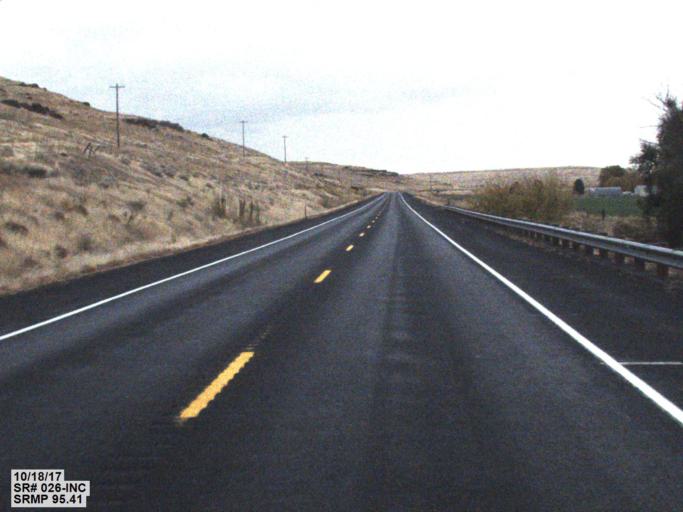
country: US
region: Washington
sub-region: Columbia County
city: Dayton
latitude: 46.7771
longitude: -118.0722
